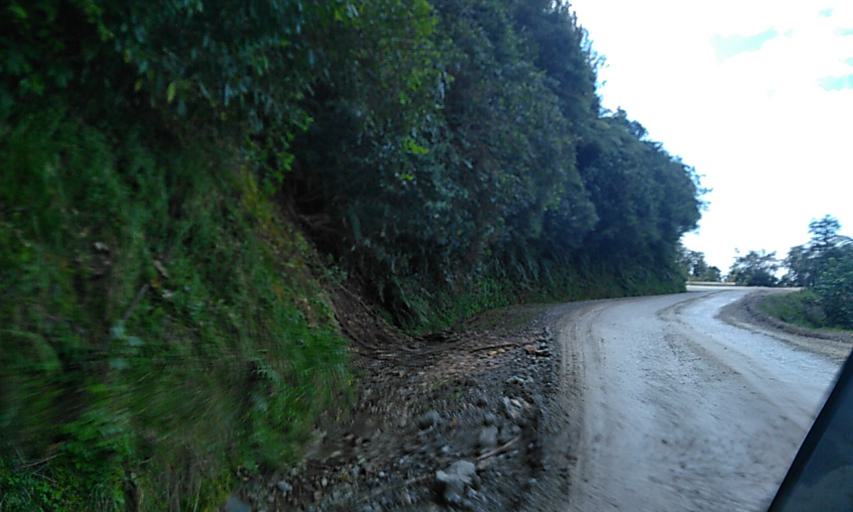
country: NZ
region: Gisborne
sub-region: Gisborne District
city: Gisborne
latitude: -38.3081
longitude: 178.0852
